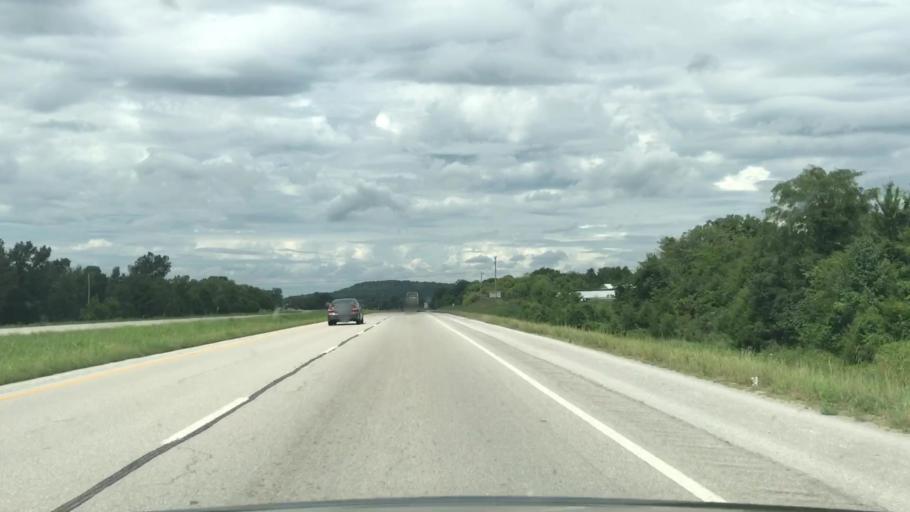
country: US
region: Kentucky
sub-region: Todd County
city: Elkton
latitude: 36.8326
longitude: -87.2304
